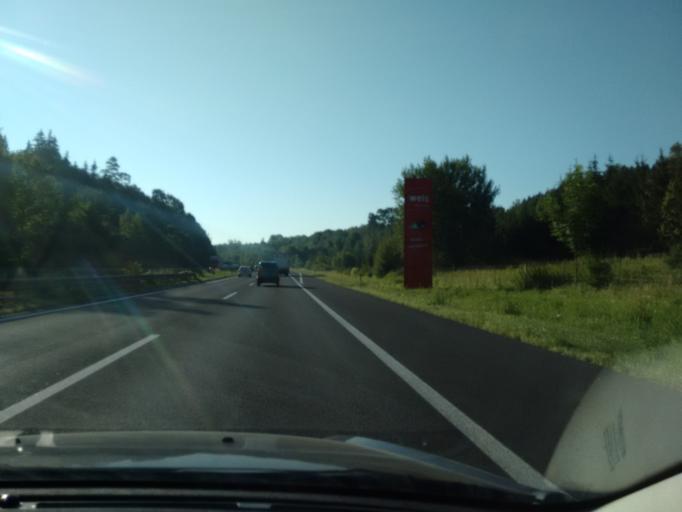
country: AT
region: Upper Austria
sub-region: Wels-Land
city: Gunskirchen
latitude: 48.1868
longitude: 13.9589
